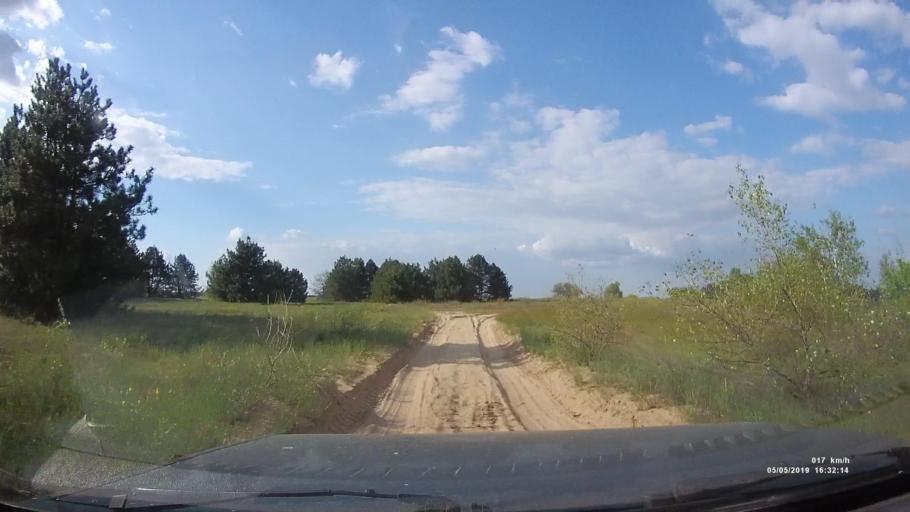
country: RU
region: Rostov
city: Ust'-Donetskiy
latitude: 47.7783
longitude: 41.0141
